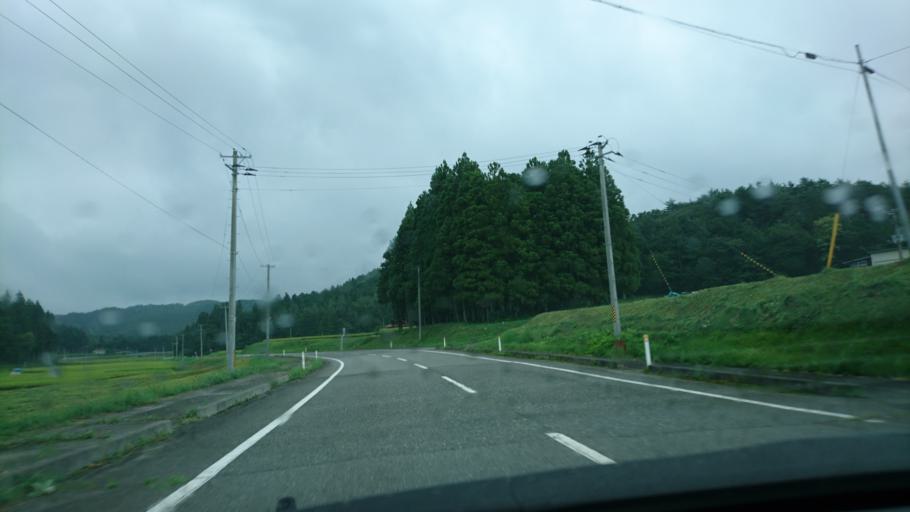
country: JP
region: Iwate
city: Ichinoseki
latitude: 38.8847
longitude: 140.9657
